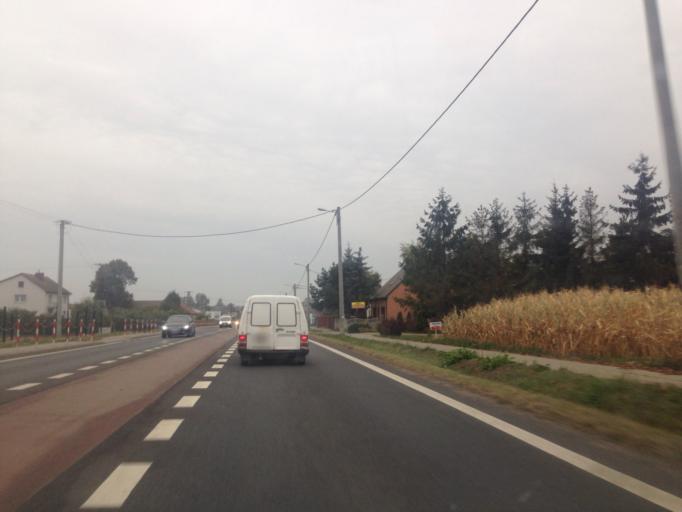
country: PL
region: Greater Poland Voivodeship
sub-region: Powiat gnieznienski
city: Lubowo
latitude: 52.5140
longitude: 17.4710
